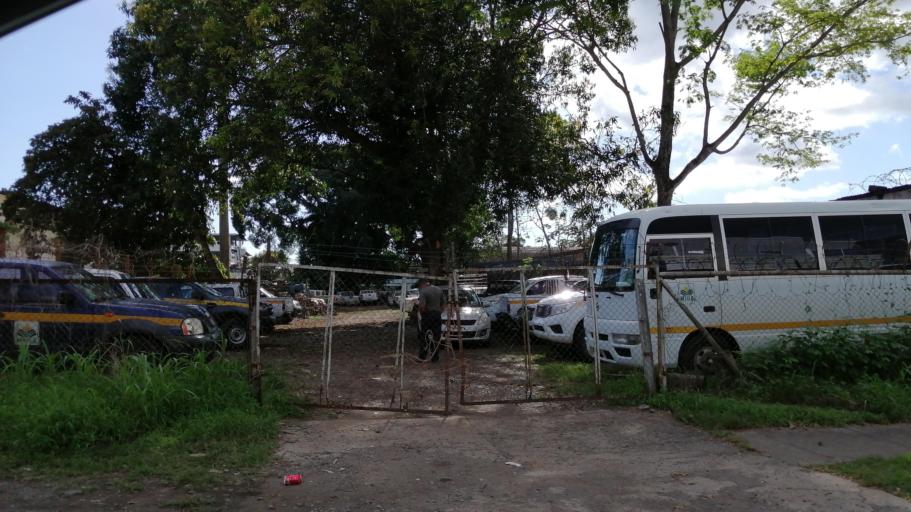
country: PA
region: Chiriqui
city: David
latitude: 8.4303
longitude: -82.4302
